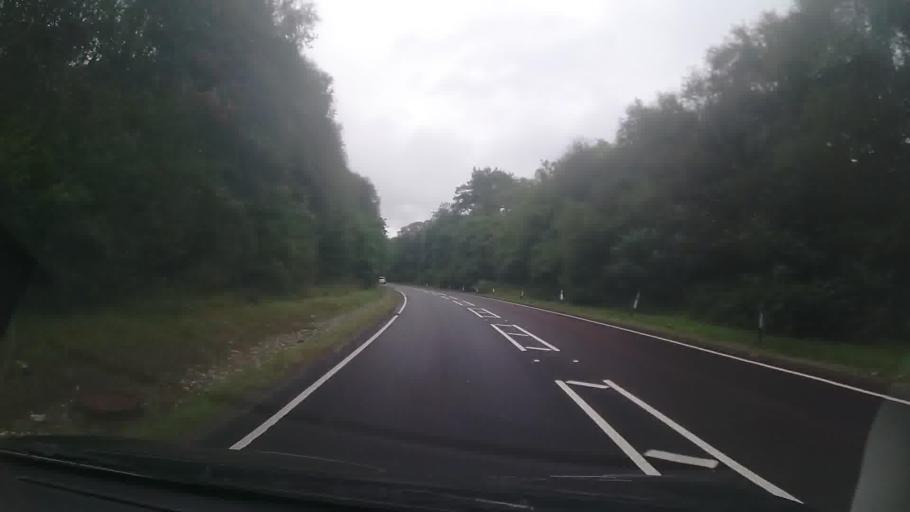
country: GB
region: Scotland
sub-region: Argyll and Bute
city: Garelochhead
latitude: 56.3453
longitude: -4.7045
